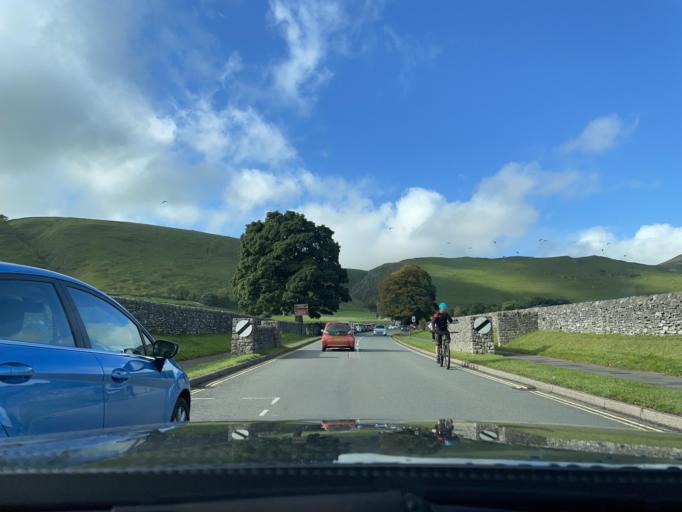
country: GB
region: England
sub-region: Derbyshire
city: Hope Valley
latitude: 53.3427
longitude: -1.7816
